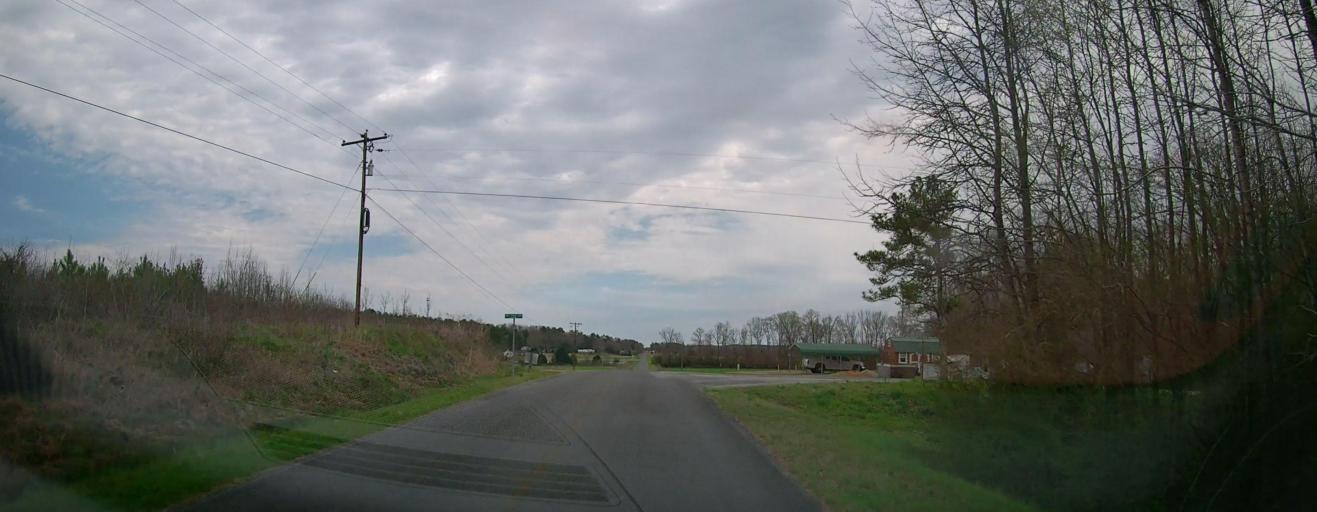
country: US
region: Alabama
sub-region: Marion County
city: Hamilton
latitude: 34.1968
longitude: -88.1629
